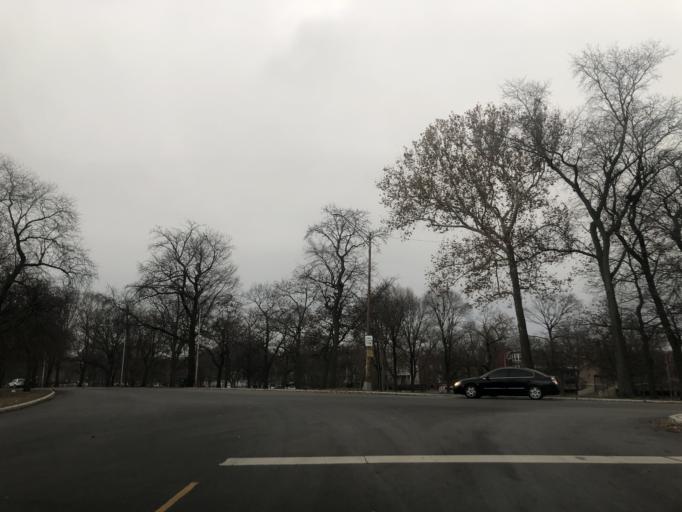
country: US
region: Illinois
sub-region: Cook County
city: Chicago
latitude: 41.7868
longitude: -87.6147
